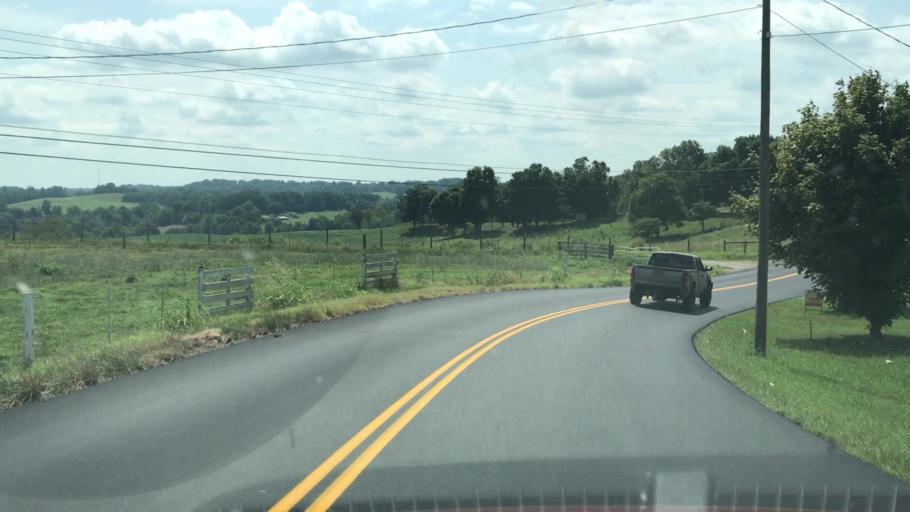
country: US
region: Kentucky
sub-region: Monroe County
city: Tompkinsville
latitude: 36.7266
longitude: -85.7231
